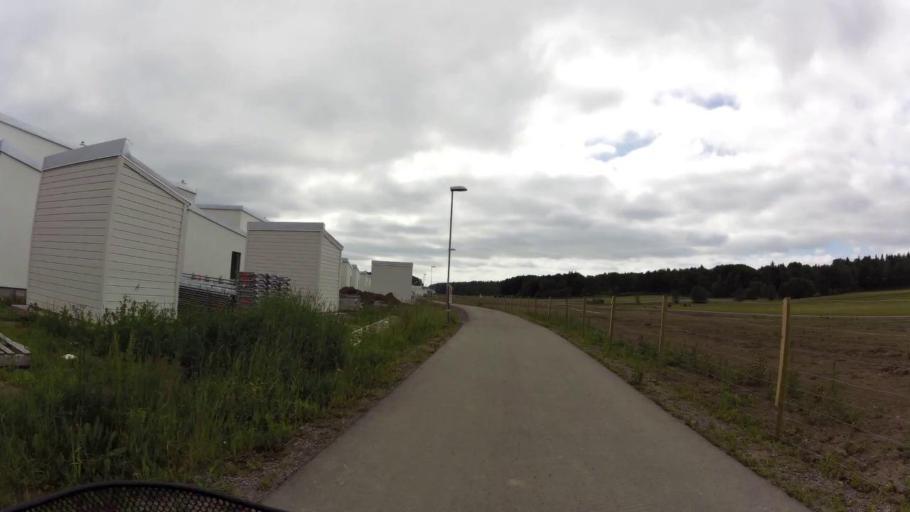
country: SE
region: OEstergoetland
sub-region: Linkopings Kommun
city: Sturefors
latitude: 58.3656
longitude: 15.6750
